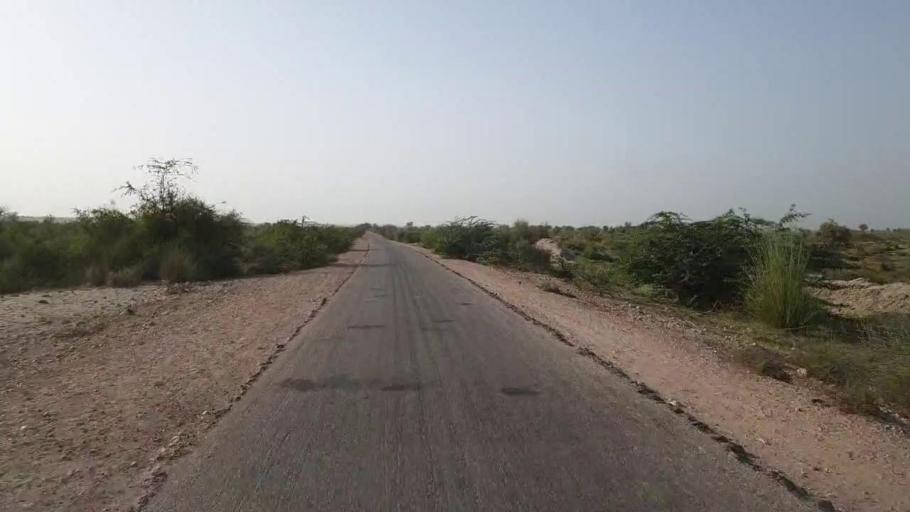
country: PK
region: Sindh
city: Jam Sahib
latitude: 26.4536
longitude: 68.8615
